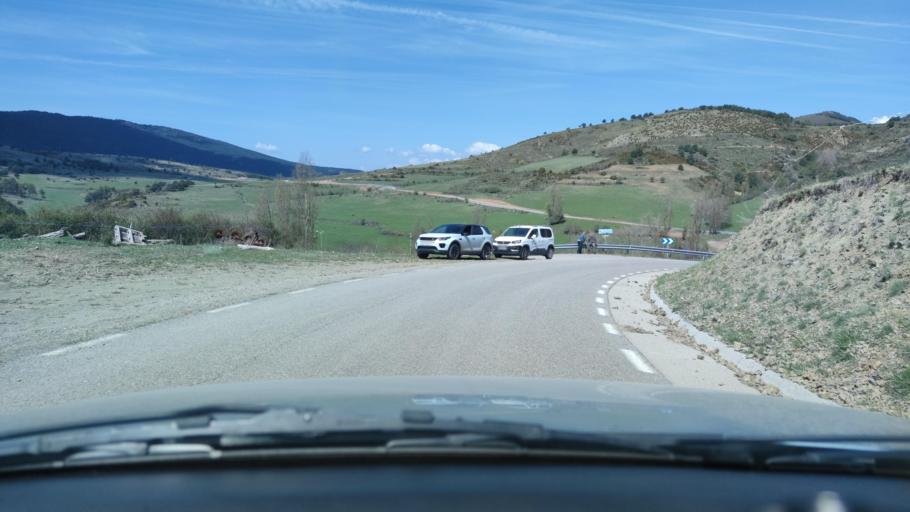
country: ES
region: Catalonia
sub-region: Provincia de Lleida
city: Coll de Nargo
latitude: 42.2828
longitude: 1.2211
